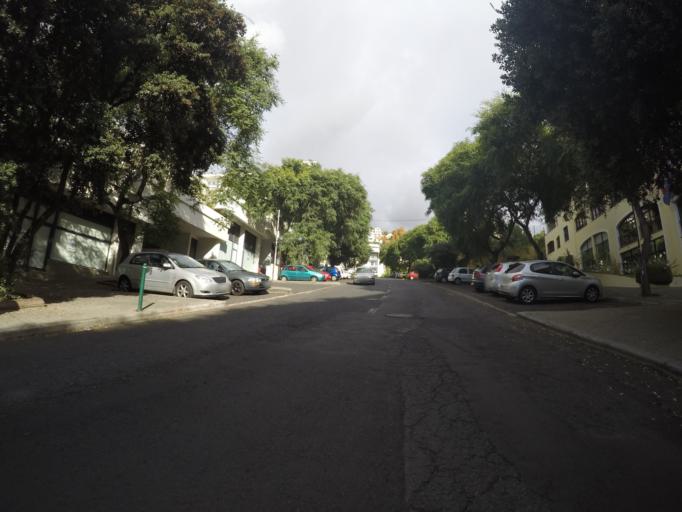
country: PT
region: Madeira
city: Camara de Lobos
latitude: 32.6371
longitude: -16.9340
